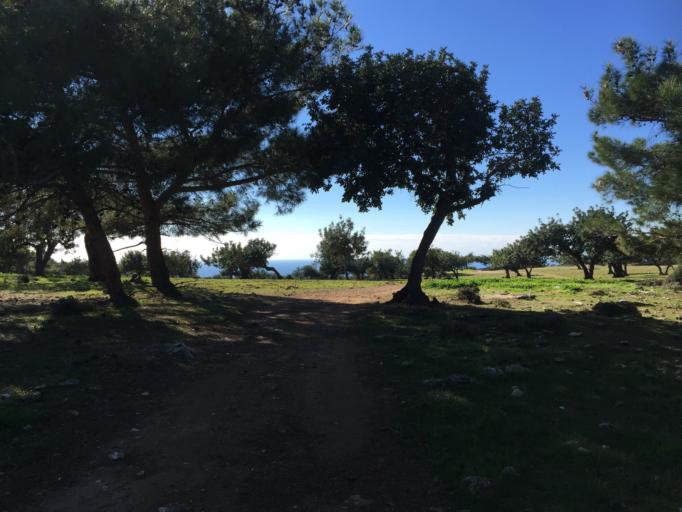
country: CY
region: Limassol
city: Pissouri
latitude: 34.6662
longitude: 32.6827
